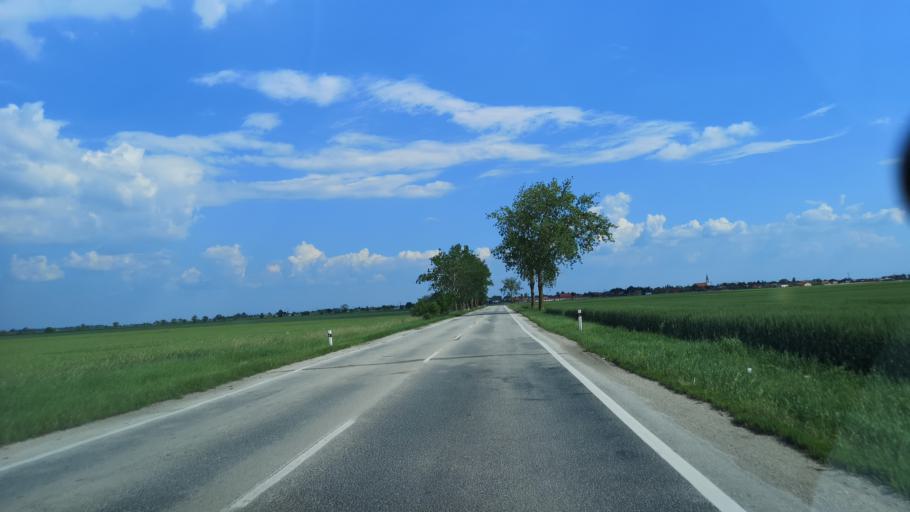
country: SK
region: Bratislavsky
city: Senec
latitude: 48.1324
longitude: 17.4109
